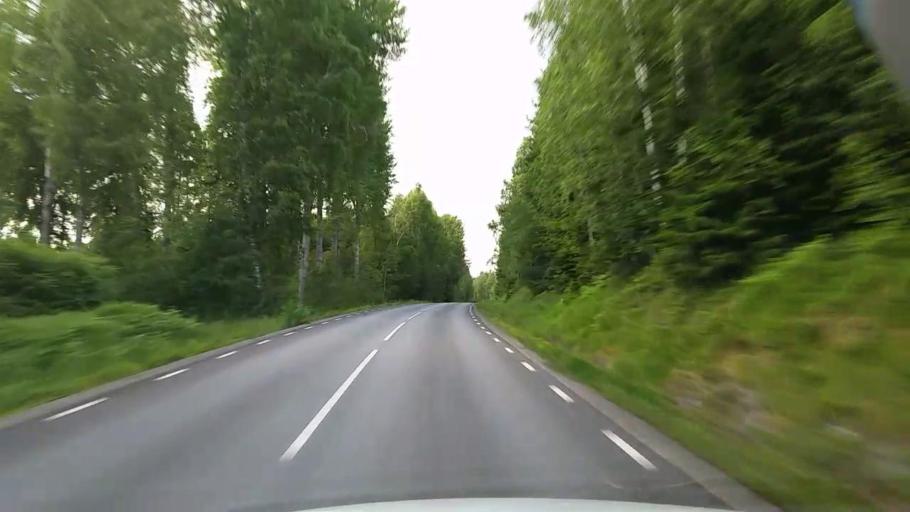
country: SE
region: Vaestmanland
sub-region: Kopings Kommun
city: Kolsva
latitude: 59.7425
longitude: 15.8272
